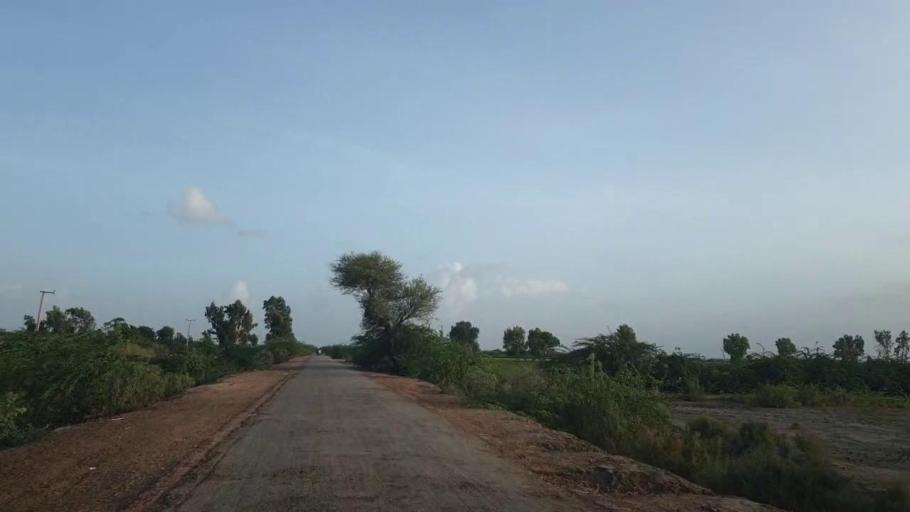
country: PK
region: Sindh
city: Kadhan
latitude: 24.6095
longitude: 69.1158
